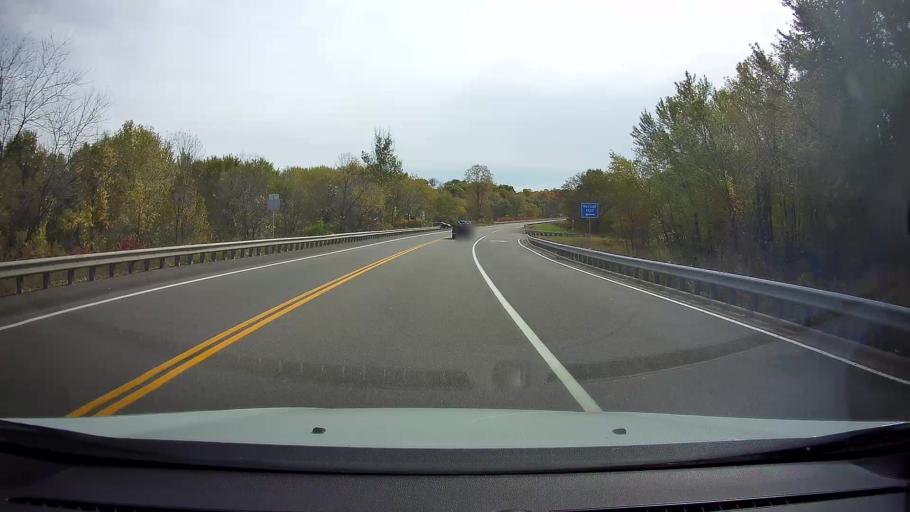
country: US
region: Wisconsin
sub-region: Polk County
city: Osceola
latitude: 45.3232
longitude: -92.7137
